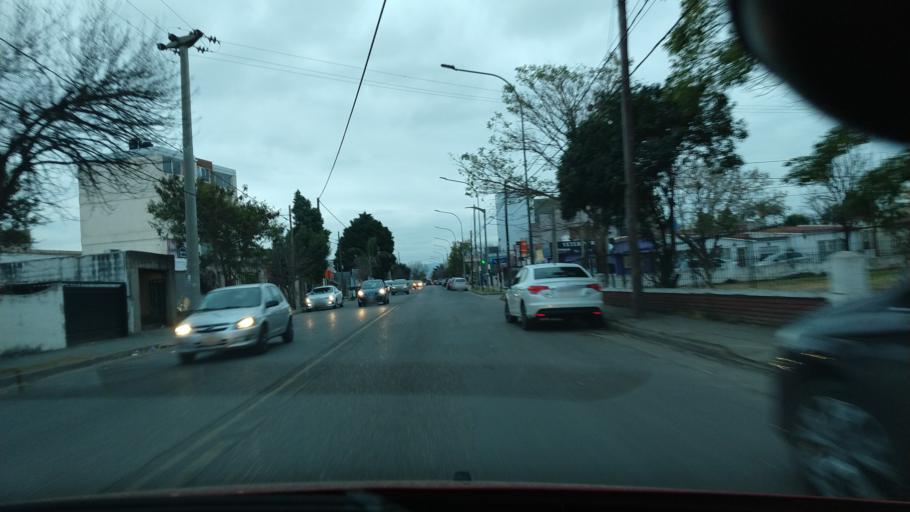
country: AR
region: Cordoba
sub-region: Departamento de Capital
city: Cordoba
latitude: -31.3609
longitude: -64.2322
